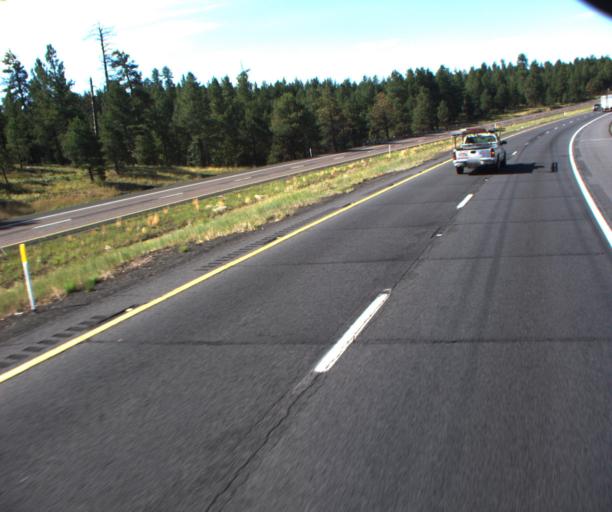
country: US
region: Arizona
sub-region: Coconino County
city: Mountainaire
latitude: 35.0701
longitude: -111.6827
